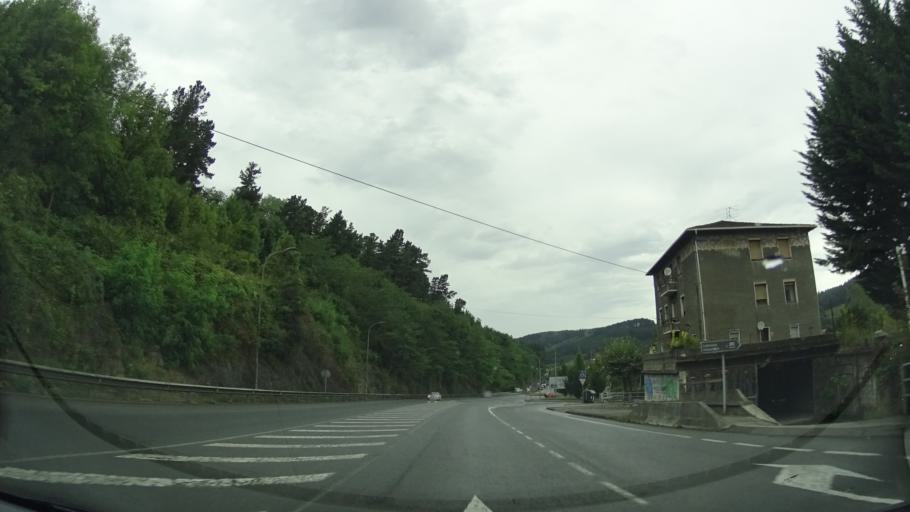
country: ES
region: Basque Country
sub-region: Bizkaia
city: Amorebieta
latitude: 43.2059
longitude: -2.7767
